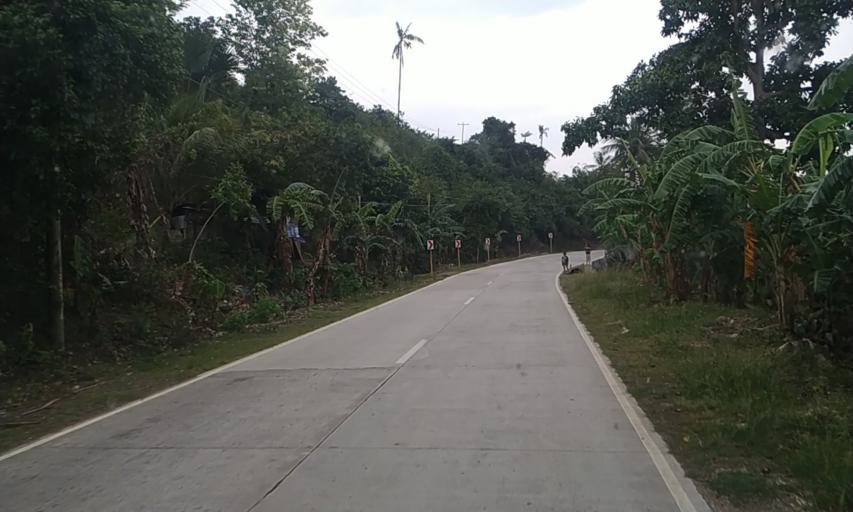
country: PH
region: Central Visayas
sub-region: Province of Negros Oriental
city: Calamba
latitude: 10.1972
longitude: 123.2955
